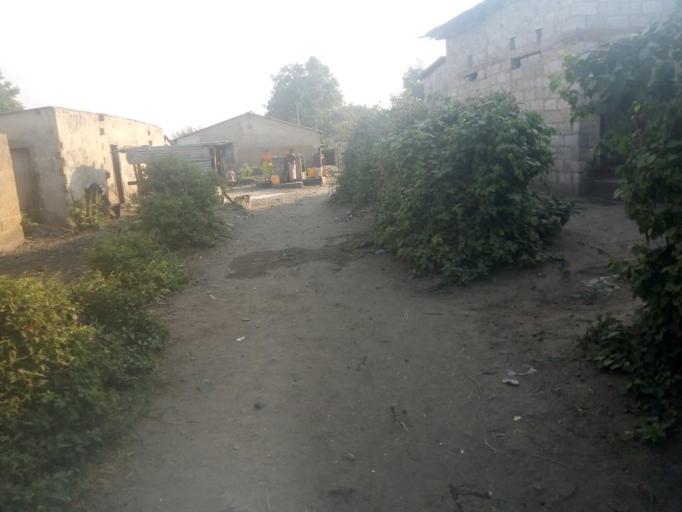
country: ZM
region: Lusaka
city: Lusaka
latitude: -15.4042
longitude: 28.3639
